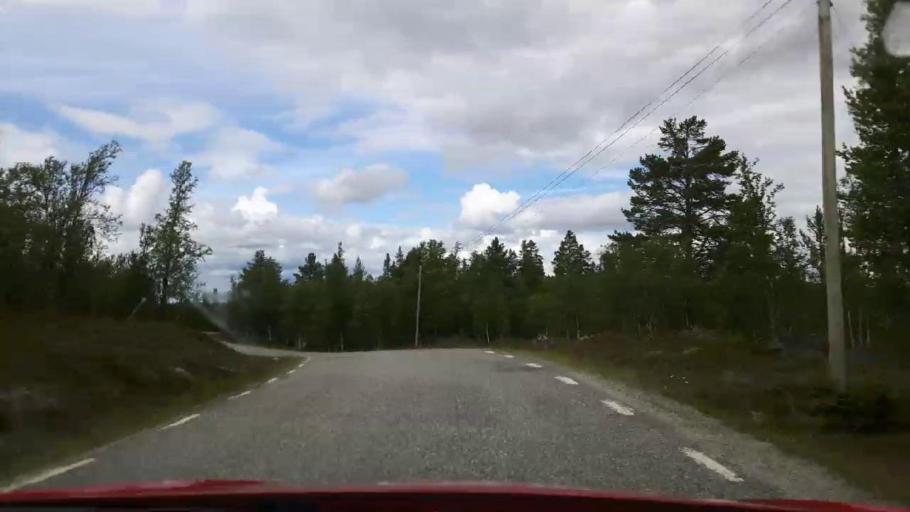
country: NO
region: Hedmark
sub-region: Engerdal
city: Engerdal
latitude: 62.3510
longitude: 12.7948
